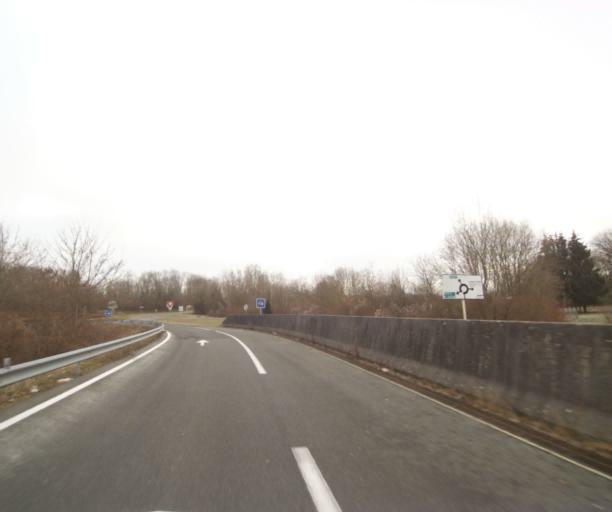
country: FR
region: Lorraine
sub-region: Departement de la Meuse
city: Ancerville
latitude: 48.6371
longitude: 5.0124
